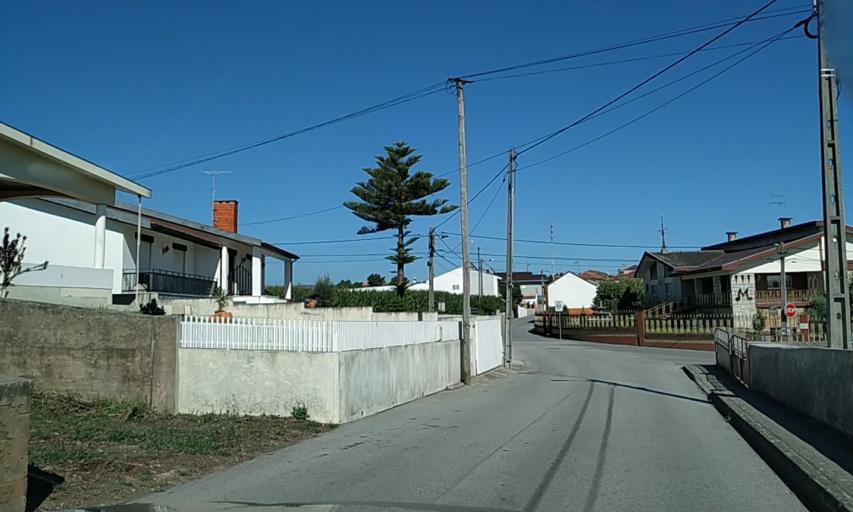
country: PT
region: Aveiro
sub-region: Estarreja
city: Salreu
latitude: 40.7497
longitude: -8.5549
